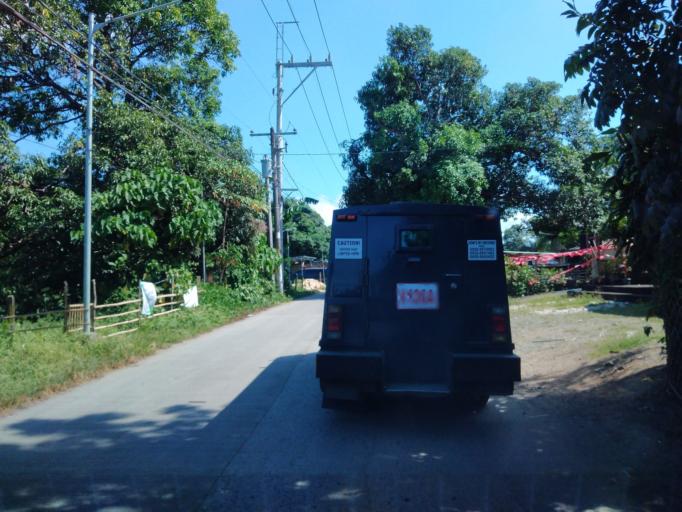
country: PH
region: Central Luzon
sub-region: Province of Bulacan
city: Balasing
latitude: 14.8599
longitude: 121.0343
